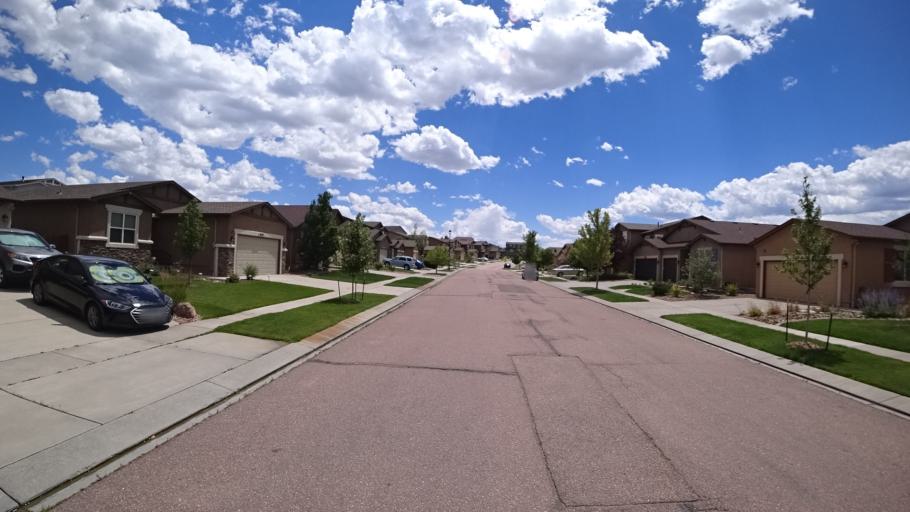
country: US
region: Colorado
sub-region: El Paso County
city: Black Forest
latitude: 38.9489
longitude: -104.7091
